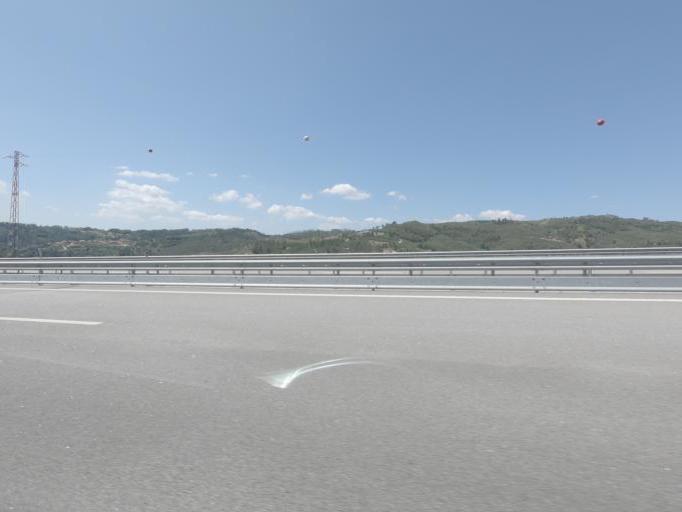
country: PT
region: Porto
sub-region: Amarante
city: Amarante
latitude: 41.2610
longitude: -8.0130
